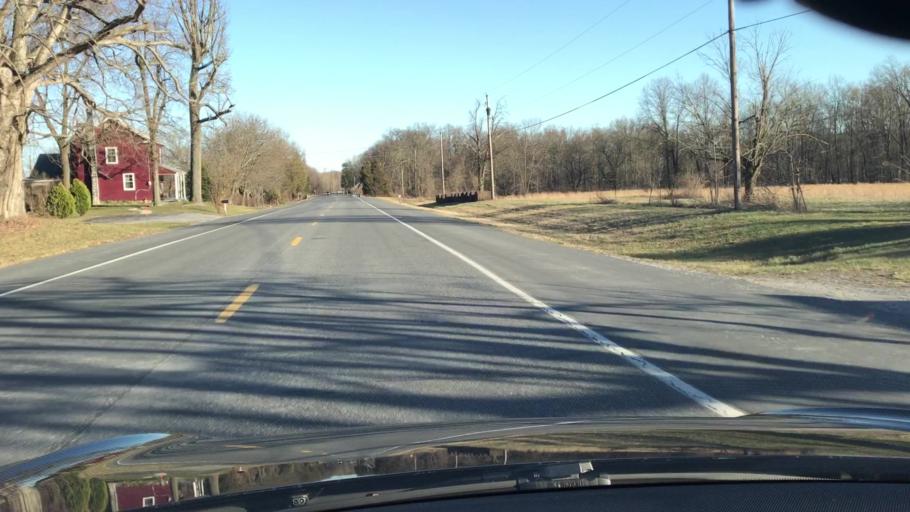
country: US
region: Pennsylvania
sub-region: York County
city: Valley Green
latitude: 40.1429
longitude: -76.8735
